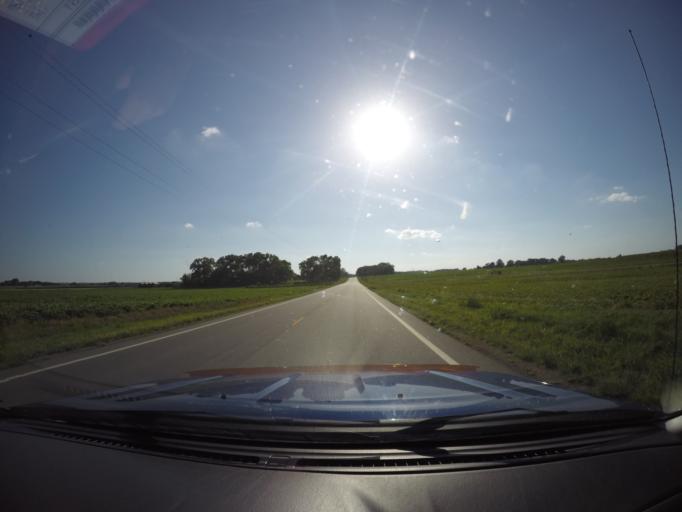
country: US
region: Kansas
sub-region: Douglas County
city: Lawrence
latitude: 39.0006
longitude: -95.2172
